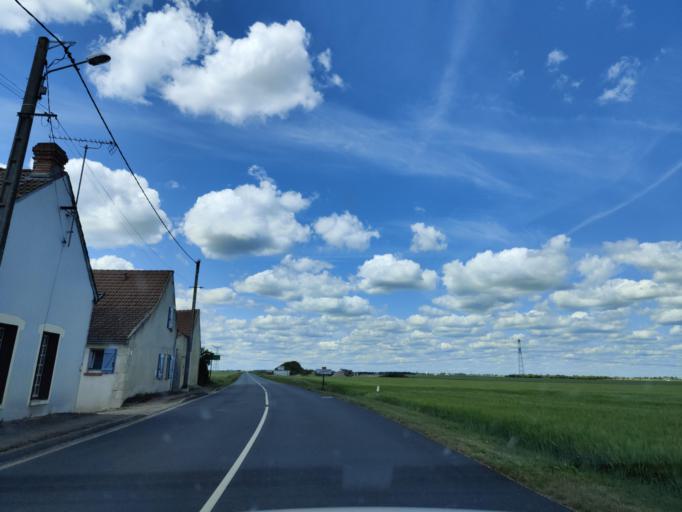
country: FR
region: Centre
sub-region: Departement du Loiret
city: Dadonville
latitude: 48.1041
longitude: 2.2678
